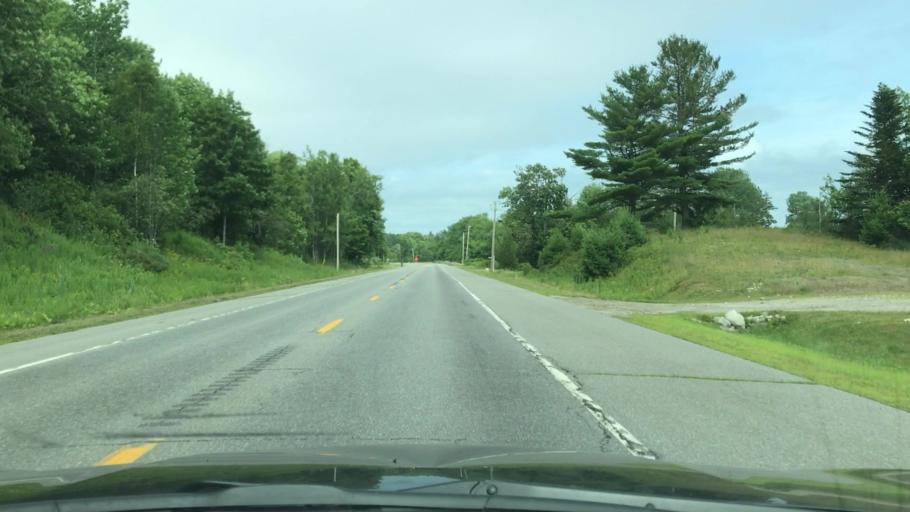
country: US
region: Maine
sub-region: Waldo County
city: Stockton Springs
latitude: 44.4957
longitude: -68.8385
